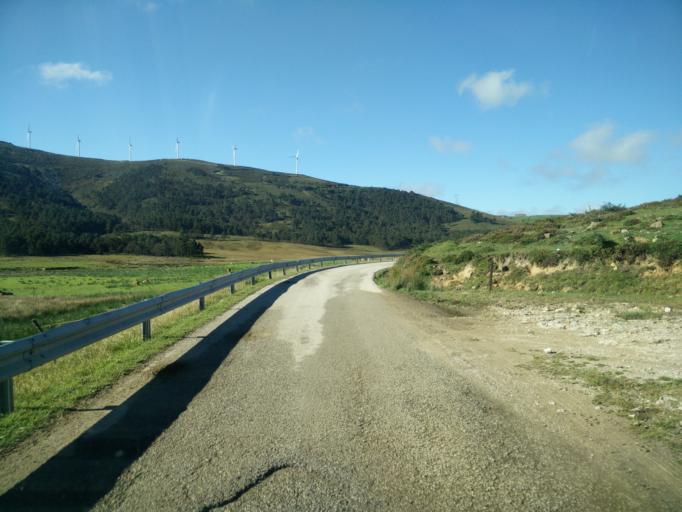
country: ES
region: Cantabria
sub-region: Provincia de Cantabria
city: San Pedro del Romeral
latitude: 43.0803
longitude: -3.8310
